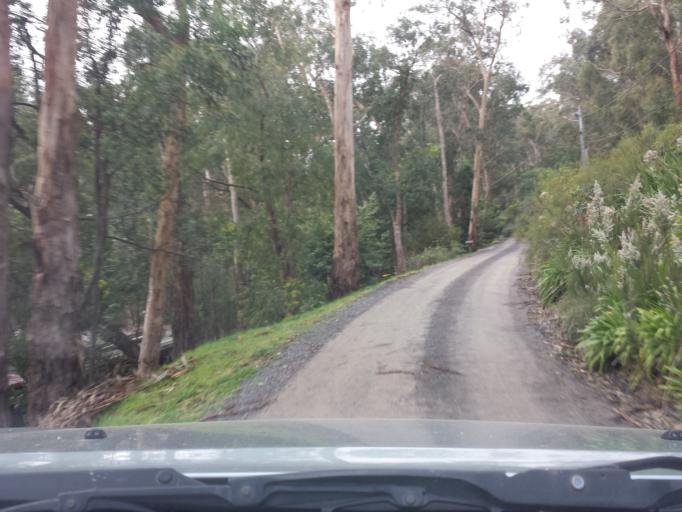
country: AU
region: Victoria
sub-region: Yarra Ranges
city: Belgrave Heights
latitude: -37.9176
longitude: 145.3664
